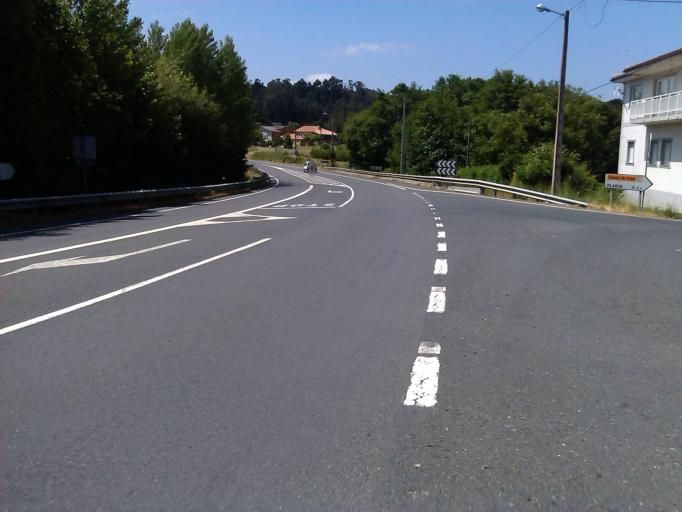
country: ES
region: Galicia
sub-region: Provincia da Coruna
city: Touro
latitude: 42.9145
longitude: -8.3560
